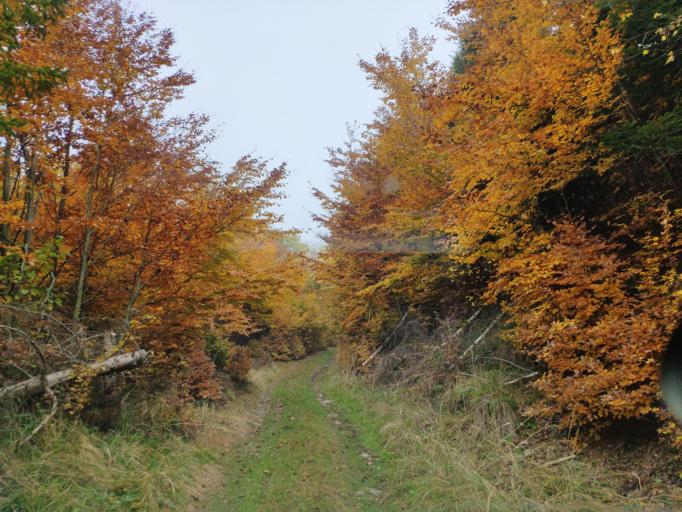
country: SK
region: Kosicky
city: Medzev
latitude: 48.7365
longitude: 20.9935
